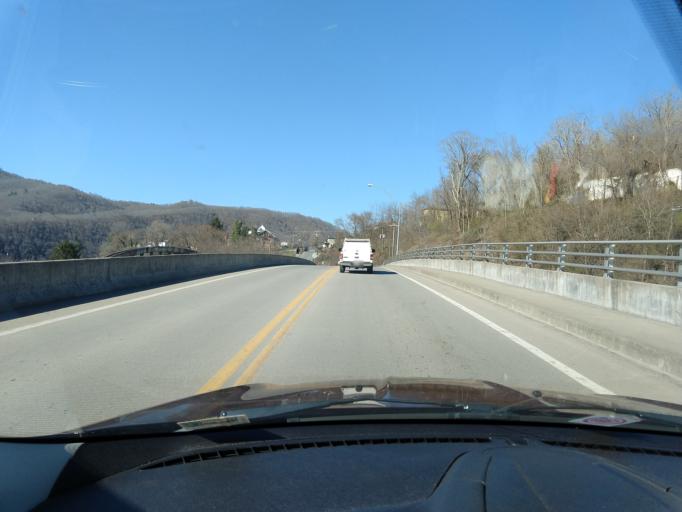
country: US
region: West Virginia
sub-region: Summers County
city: Hinton
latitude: 37.6699
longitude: -80.8918
